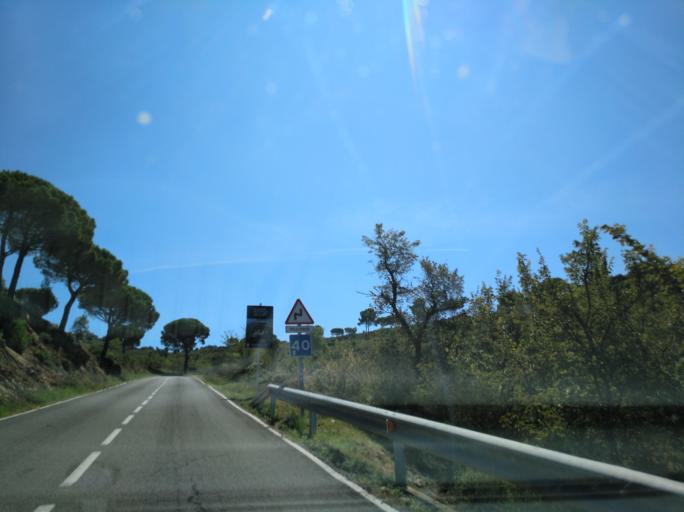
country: ES
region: Catalonia
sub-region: Provincia de Girona
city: Pau
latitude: 42.3322
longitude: 3.1305
